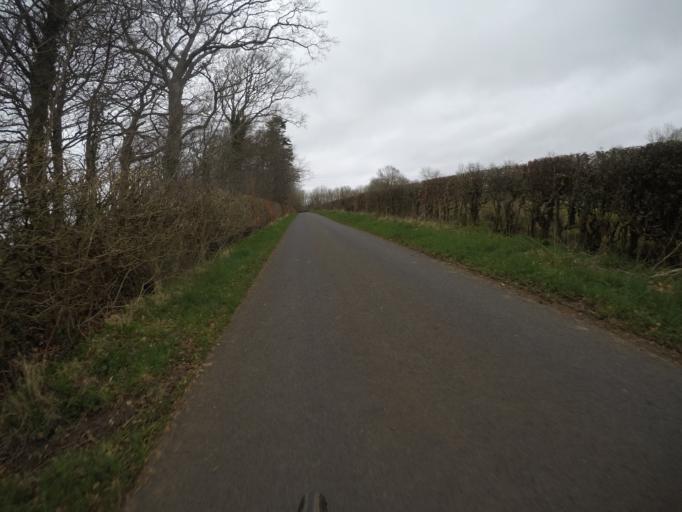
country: GB
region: Scotland
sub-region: East Ayrshire
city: Newmilns
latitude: 55.6165
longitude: -4.3539
